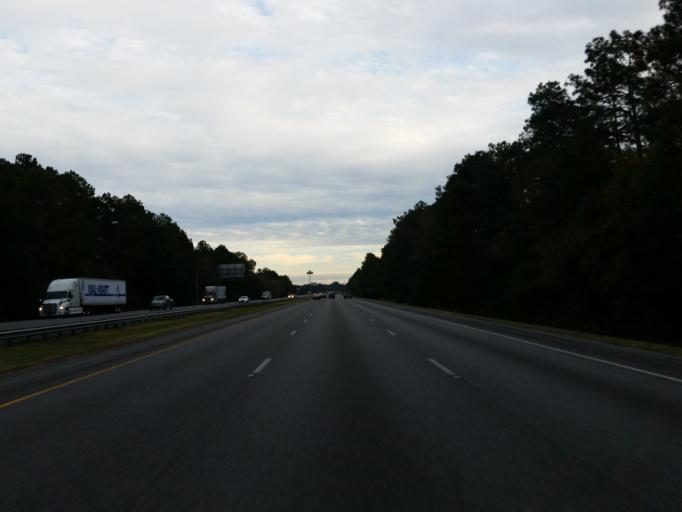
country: US
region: Georgia
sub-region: Lowndes County
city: Valdosta
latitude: 30.7638
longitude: -83.2845
